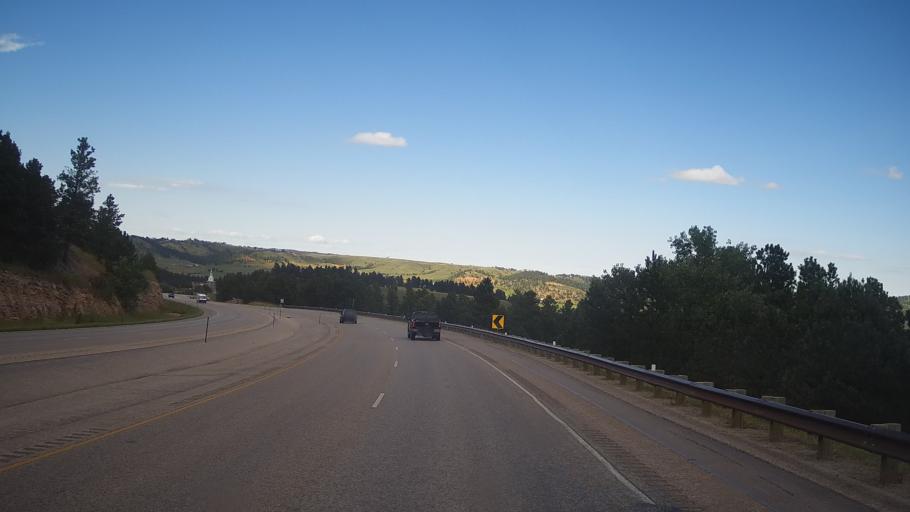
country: US
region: South Dakota
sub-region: Pennington County
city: Colonial Pine Hills
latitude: 43.9746
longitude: -103.2777
